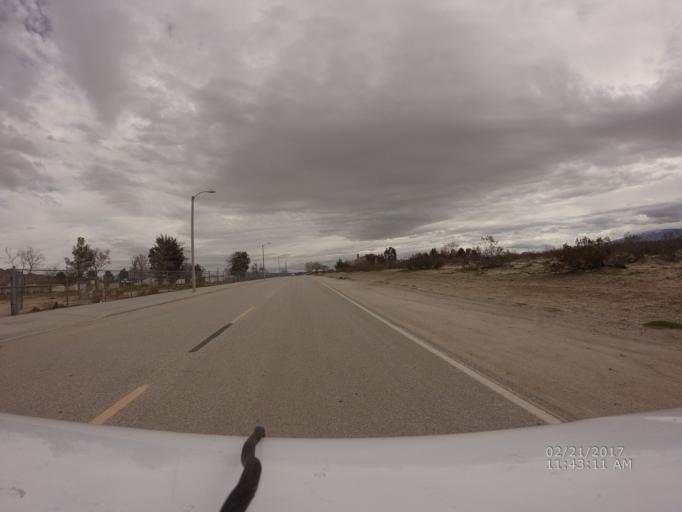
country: US
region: California
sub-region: Los Angeles County
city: Lake Los Angeles
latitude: 34.6385
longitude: -117.8304
